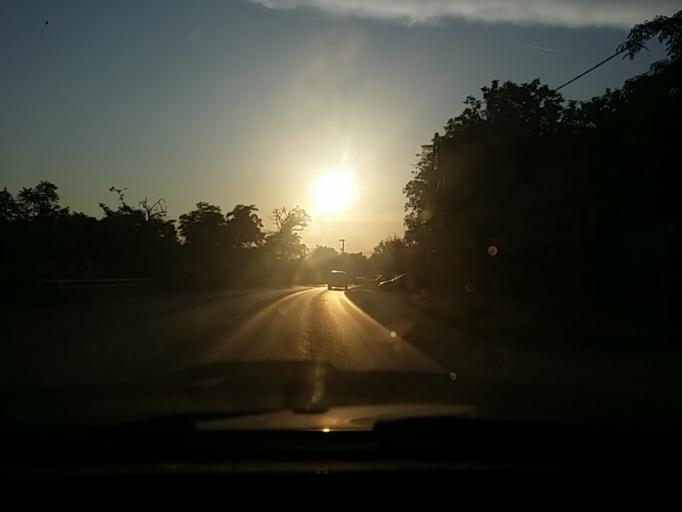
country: HU
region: Pest
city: Pilisborosjeno
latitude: 47.5884
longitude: 18.9905
